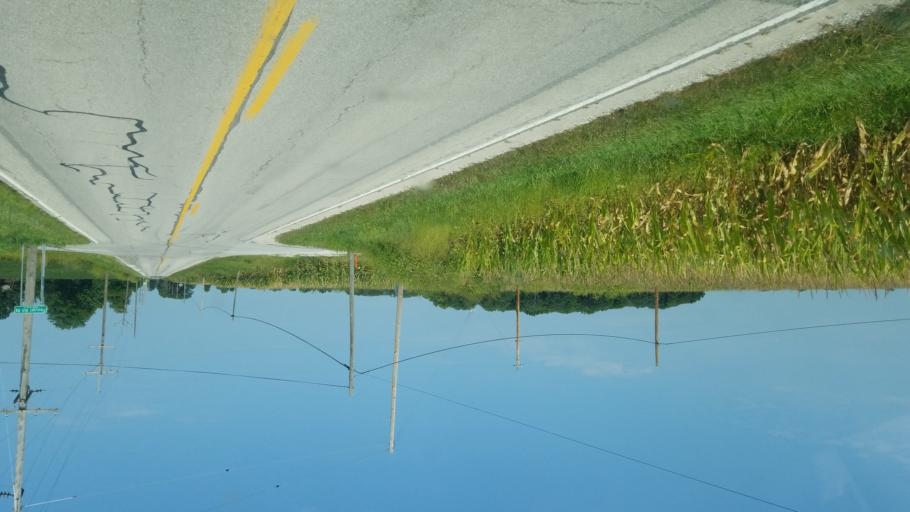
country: US
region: Ohio
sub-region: Marion County
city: Marion
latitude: 40.6293
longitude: -83.2172
